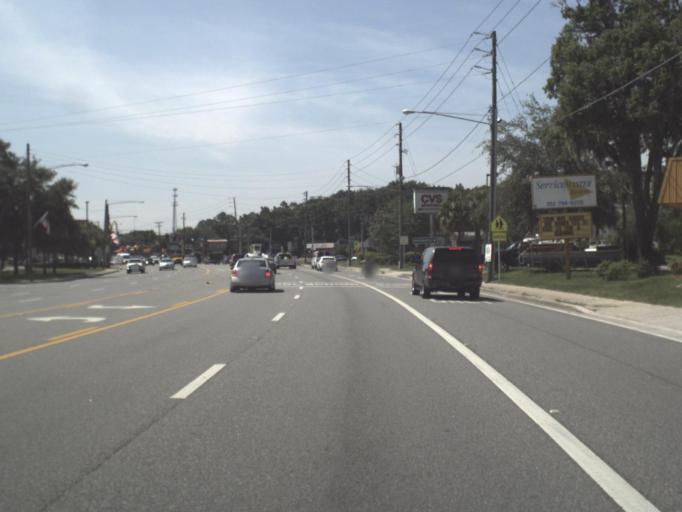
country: US
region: Florida
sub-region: Citrus County
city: Crystal River
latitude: 28.8967
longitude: -82.5852
